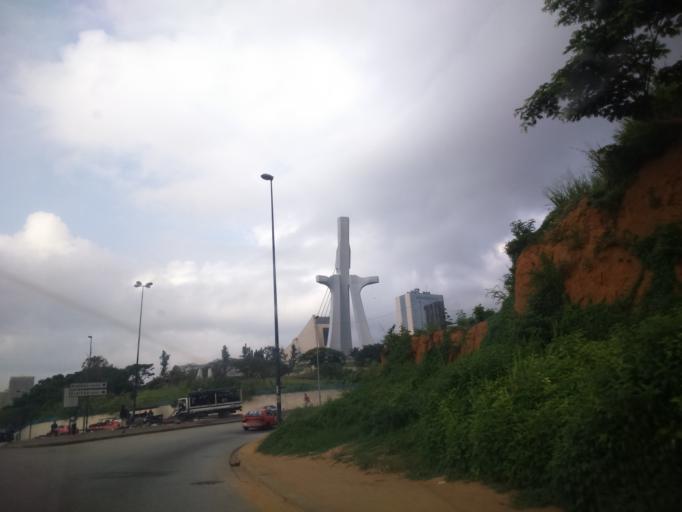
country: CI
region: Lagunes
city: Abidjan
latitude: 5.3354
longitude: -4.0187
